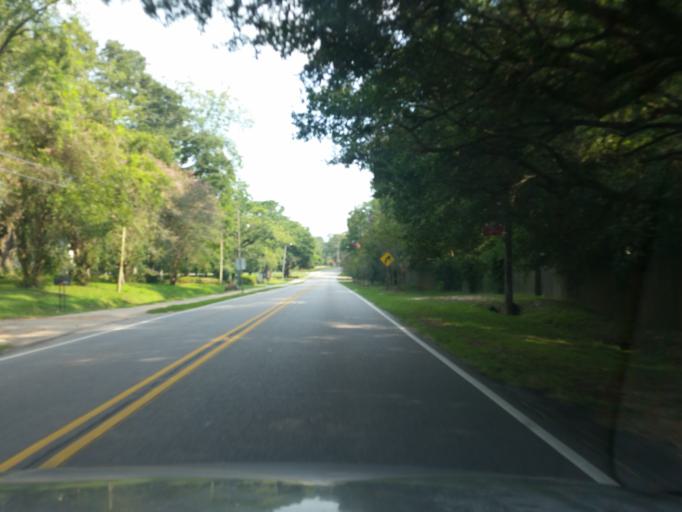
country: US
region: Alabama
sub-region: Baldwin County
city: Daphne
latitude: 30.5865
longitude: -87.9028
